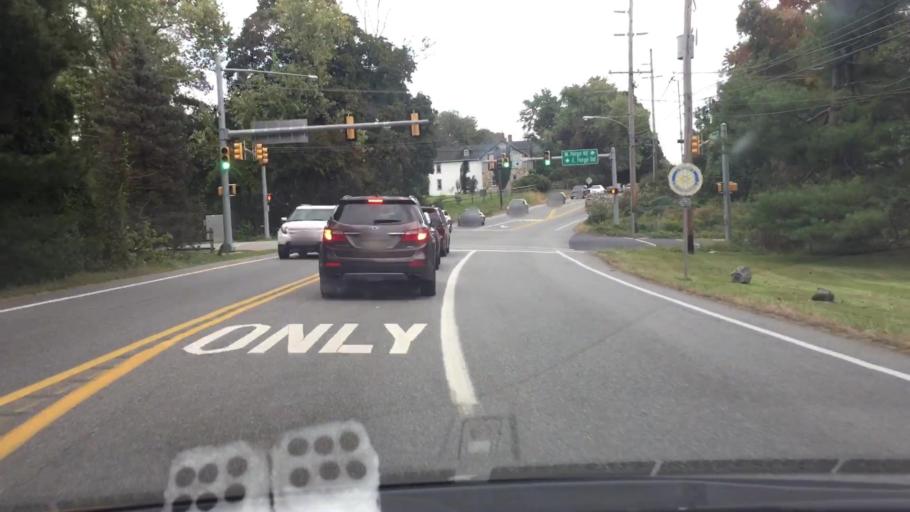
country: US
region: Pennsylvania
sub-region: Delaware County
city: Lima
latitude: 39.9330
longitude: -75.4491
